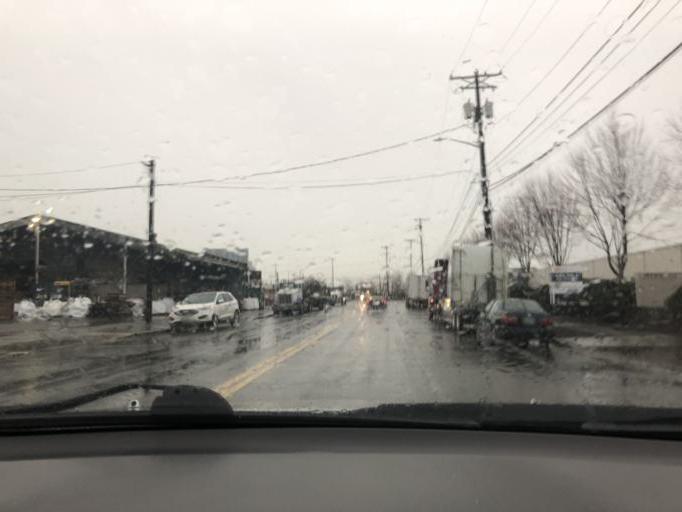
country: US
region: Washington
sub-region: Pierce County
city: Tacoma
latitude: 47.2519
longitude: -122.4231
